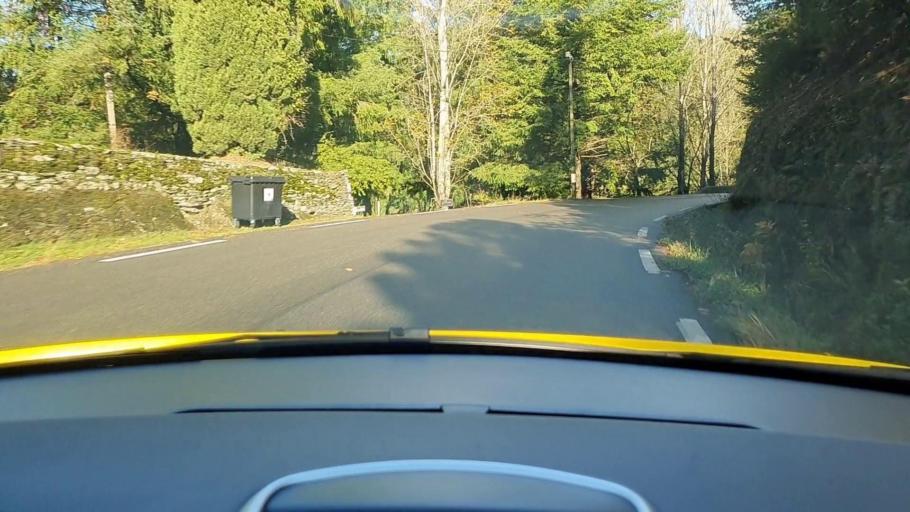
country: FR
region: Languedoc-Roussillon
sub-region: Departement du Gard
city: Valleraugue
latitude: 44.1328
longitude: 3.7549
